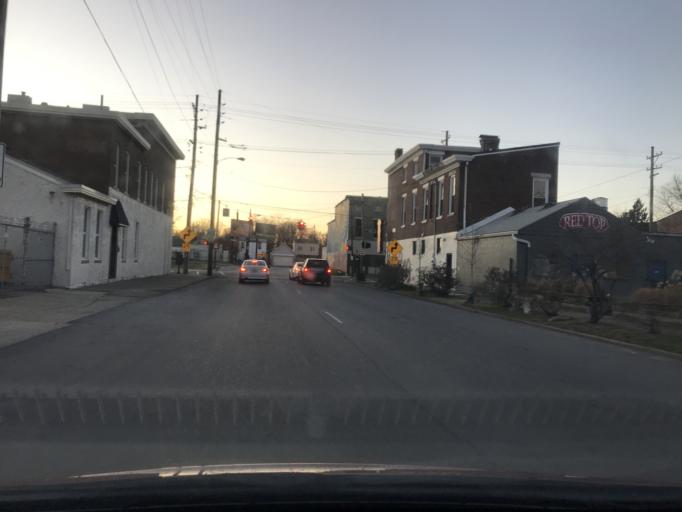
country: US
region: Kentucky
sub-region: Jefferson County
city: Louisville
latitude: 38.2341
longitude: -85.7392
